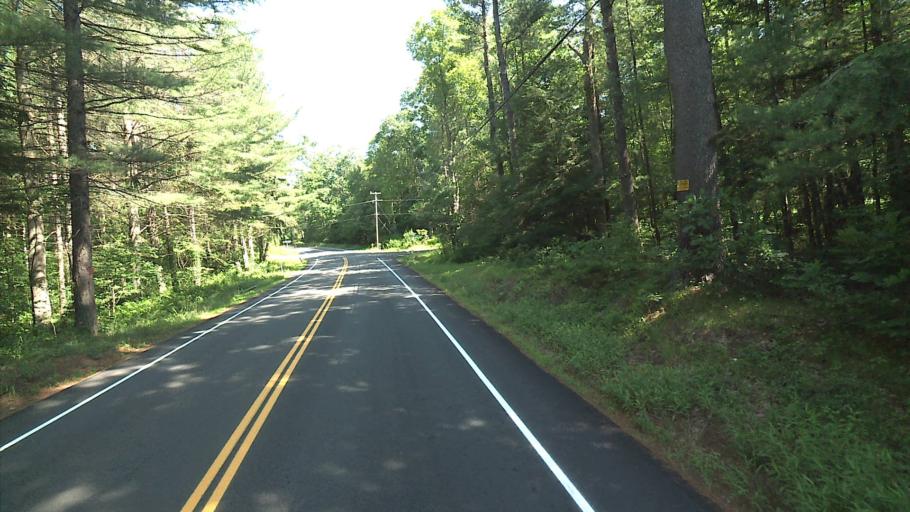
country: US
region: Connecticut
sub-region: Litchfield County
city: Terryville
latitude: 41.7313
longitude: -73.0145
